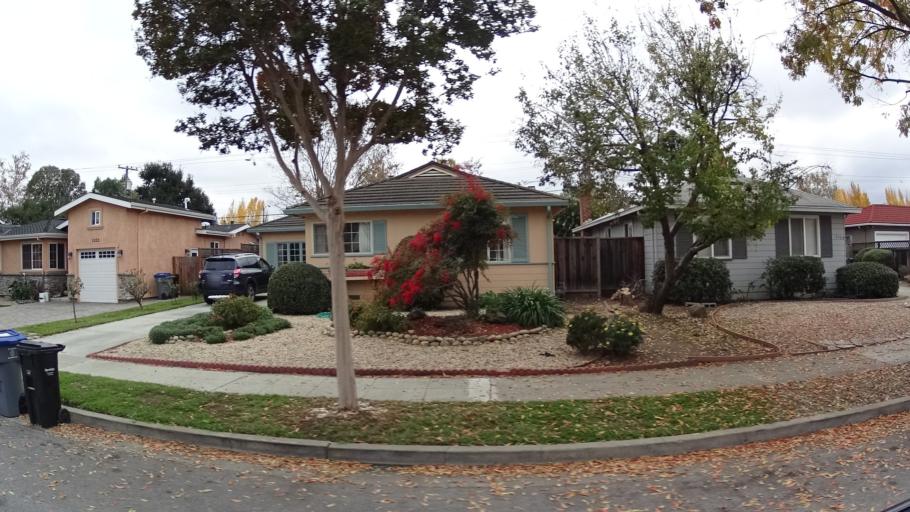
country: US
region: California
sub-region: Santa Clara County
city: Sunnyvale
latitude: 37.3689
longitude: -122.0588
